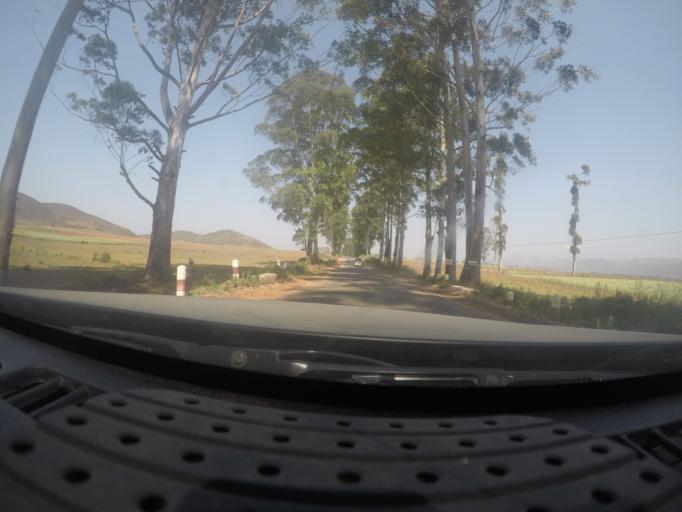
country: MM
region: Shan
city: Taunggyi
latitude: 20.8644
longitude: 96.5877
